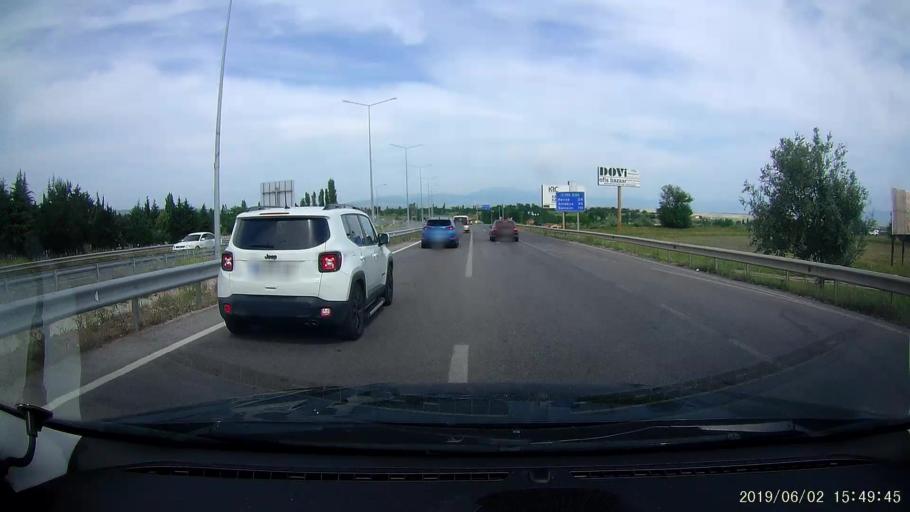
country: TR
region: Amasya
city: Merzifon
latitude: 40.8572
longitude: 35.4679
